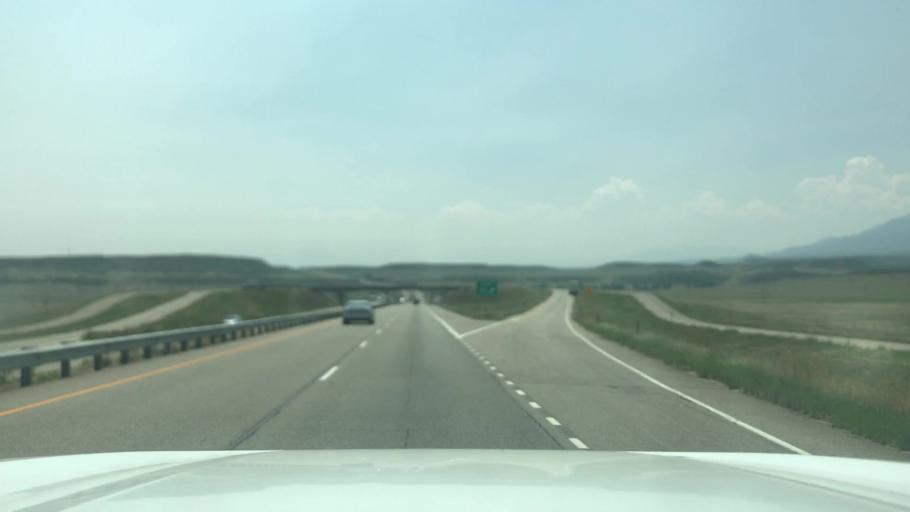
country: US
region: Colorado
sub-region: Pueblo County
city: Colorado City
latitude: 37.9281
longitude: -104.8209
